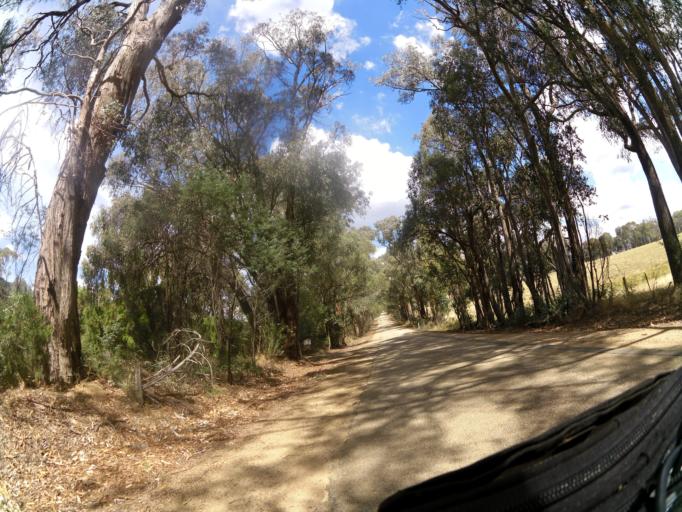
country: AU
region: Victoria
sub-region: Benalla
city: Benalla
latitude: -36.7757
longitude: 145.9741
